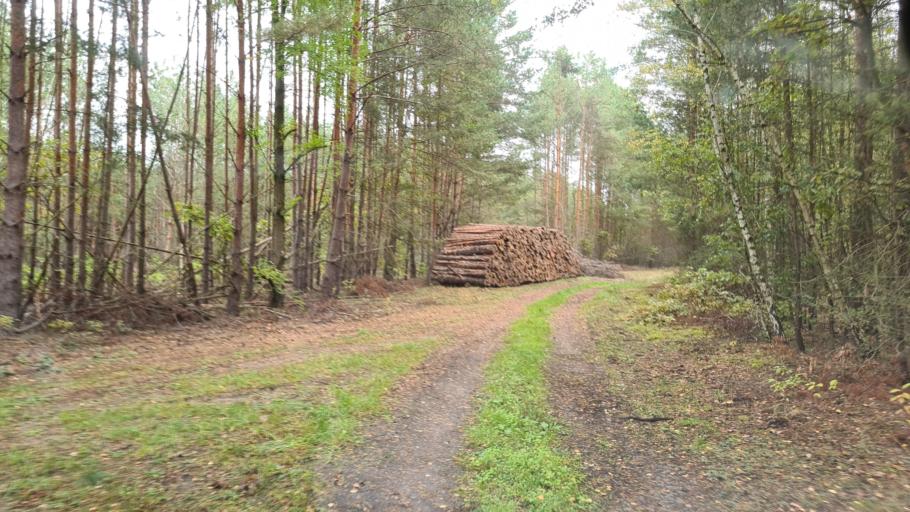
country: DE
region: Brandenburg
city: Altdobern
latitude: 51.6757
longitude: 14.1077
